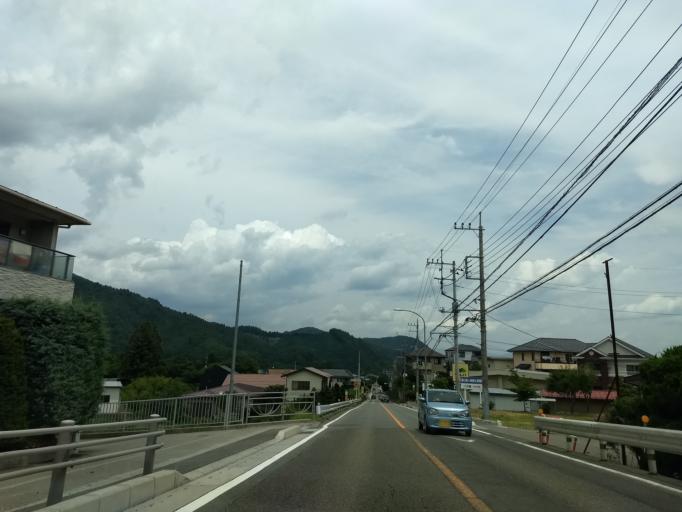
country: JP
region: Yamanashi
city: Otsuki
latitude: 35.5138
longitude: 138.8323
